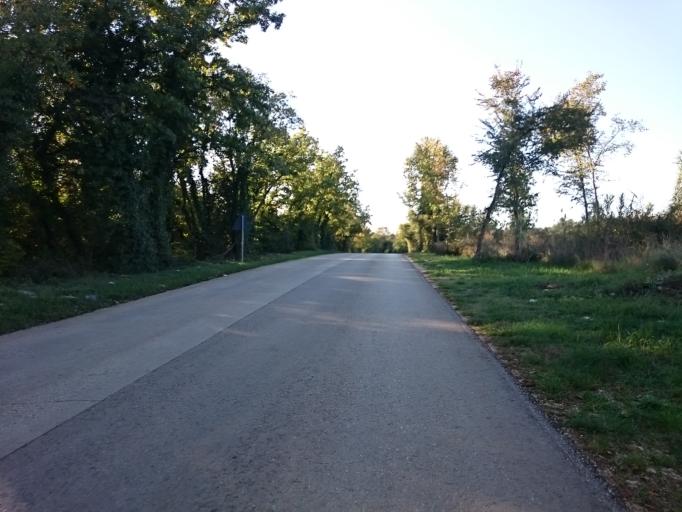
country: HR
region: Istarska
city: Novigrad
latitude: 45.2950
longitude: 13.6343
